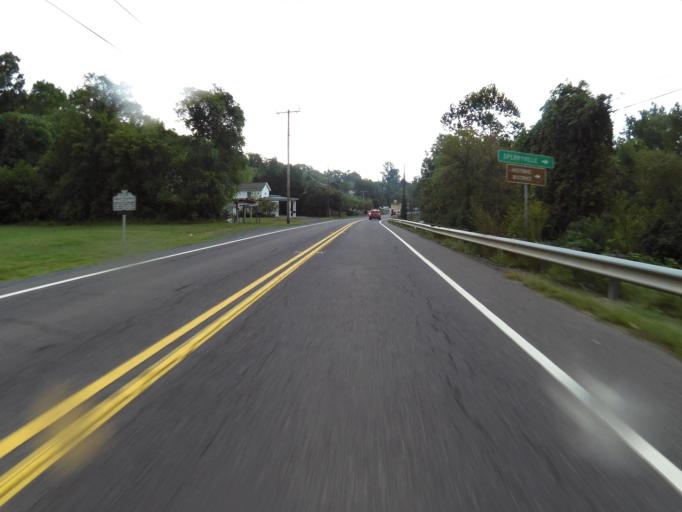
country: US
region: Virginia
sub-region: Rappahannock County
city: Washington
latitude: 38.6585
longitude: -78.2327
